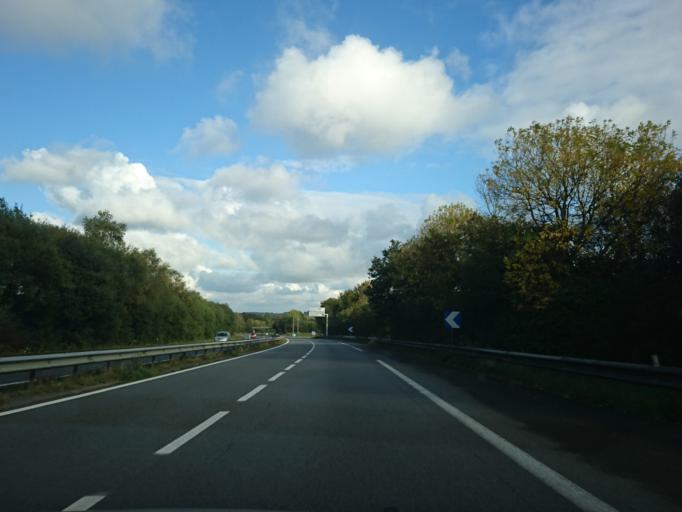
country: FR
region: Brittany
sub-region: Departement des Cotes-d'Armor
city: Louargat
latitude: 48.5676
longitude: -3.2982
